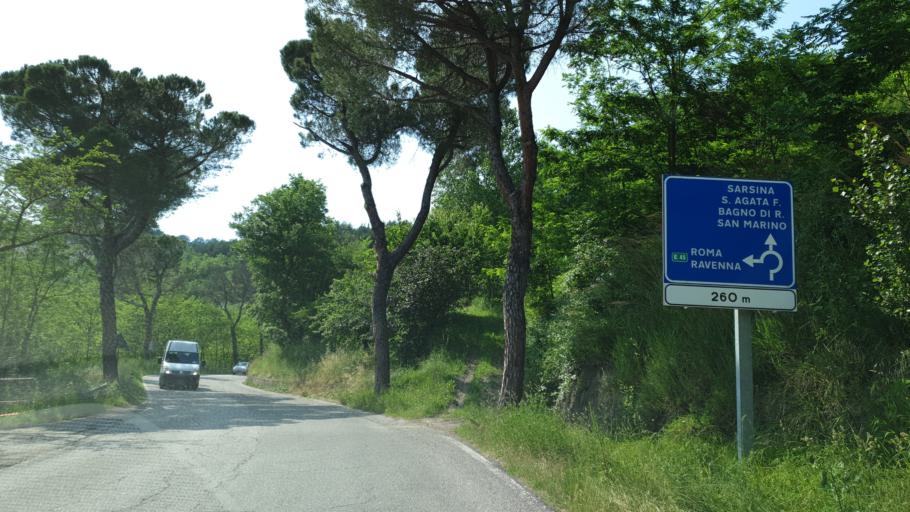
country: IT
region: Emilia-Romagna
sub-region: Forli-Cesena
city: Sarsina
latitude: 43.9250
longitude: 12.1531
